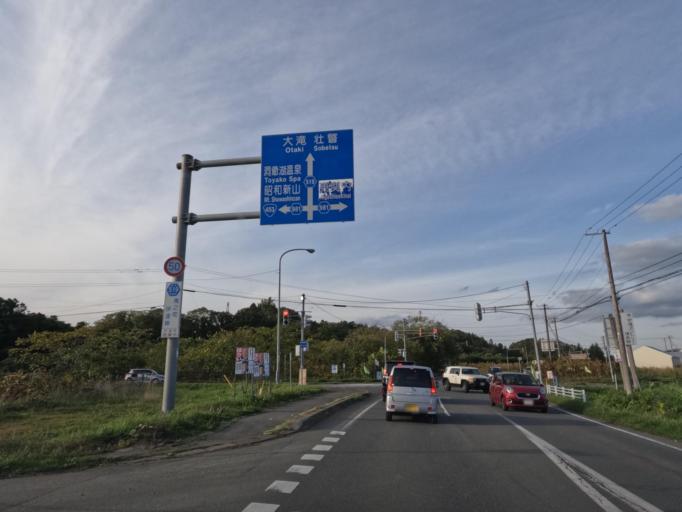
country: JP
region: Hokkaido
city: Date
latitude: 42.5045
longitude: 140.8742
